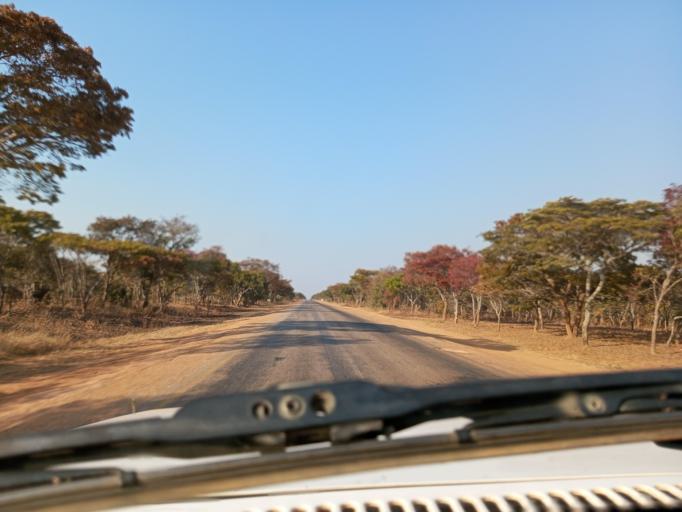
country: ZM
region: Northern
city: Mpika
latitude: -12.3807
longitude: 31.0979
